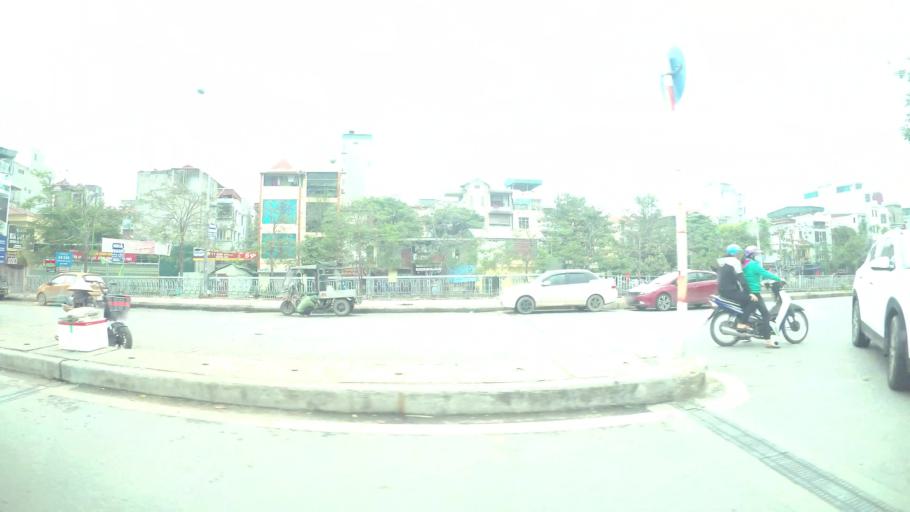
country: VN
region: Ha Noi
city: Hai BaTrung
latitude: 20.9818
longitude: 105.8457
